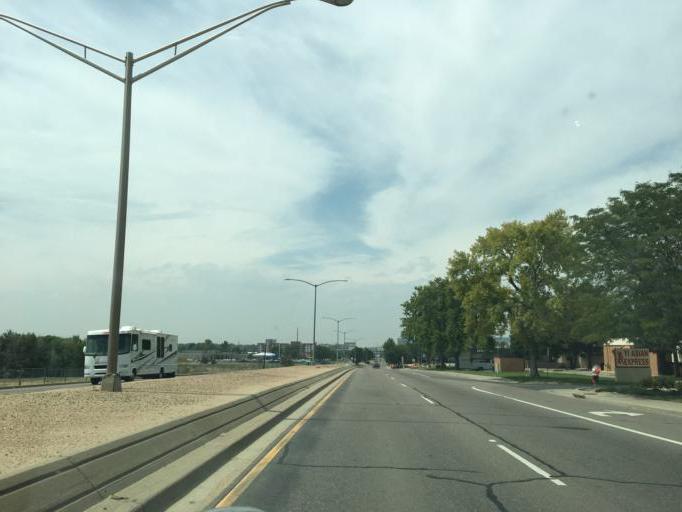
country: US
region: Colorado
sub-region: Adams County
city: Aurora
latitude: 39.7401
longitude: -104.8124
